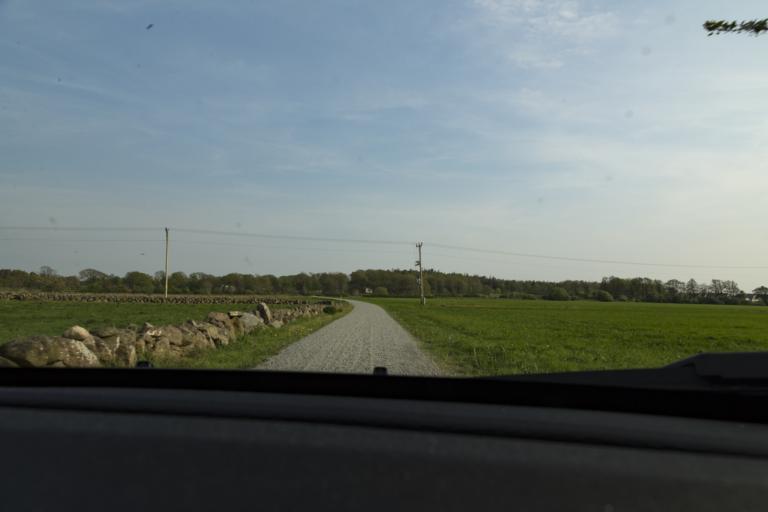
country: SE
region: Halland
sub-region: Varbergs Kommun
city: Varberg
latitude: 57.1592
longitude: 12.2608
